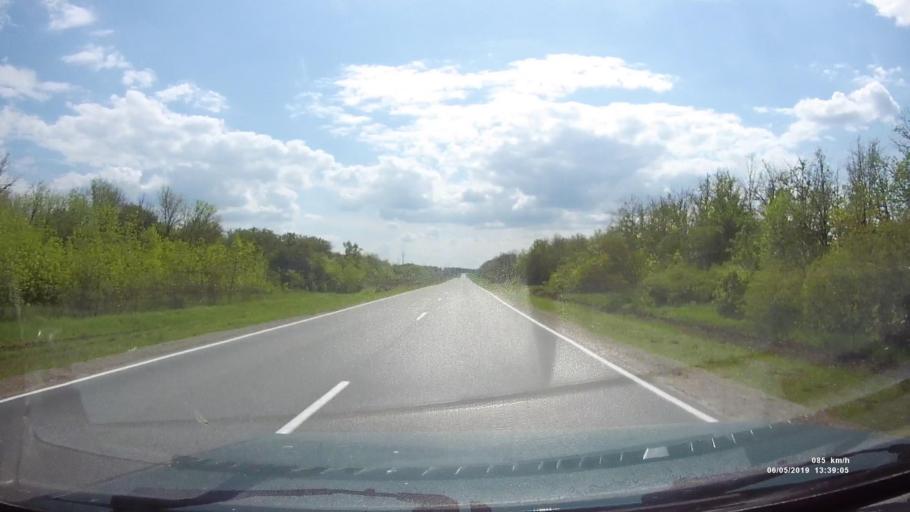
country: RU
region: Rostov
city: Ust'-Donetskiy
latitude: 47.6799
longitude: 40.7056
